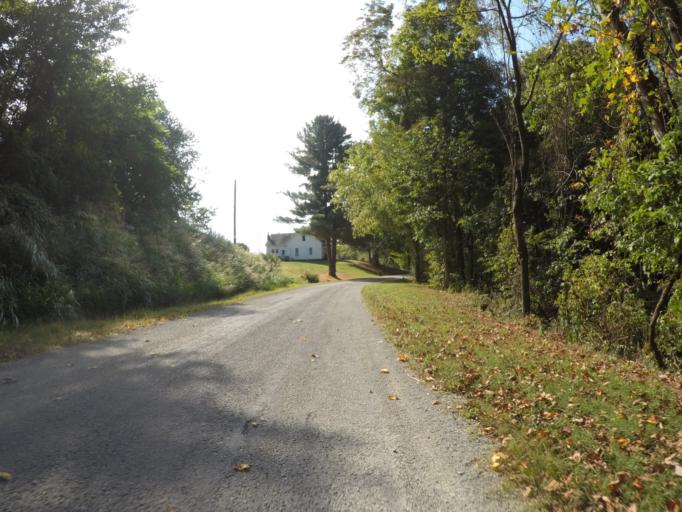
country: US
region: West Virginia
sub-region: Cabell County
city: Lesage
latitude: 38.6396
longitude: -82.4024
